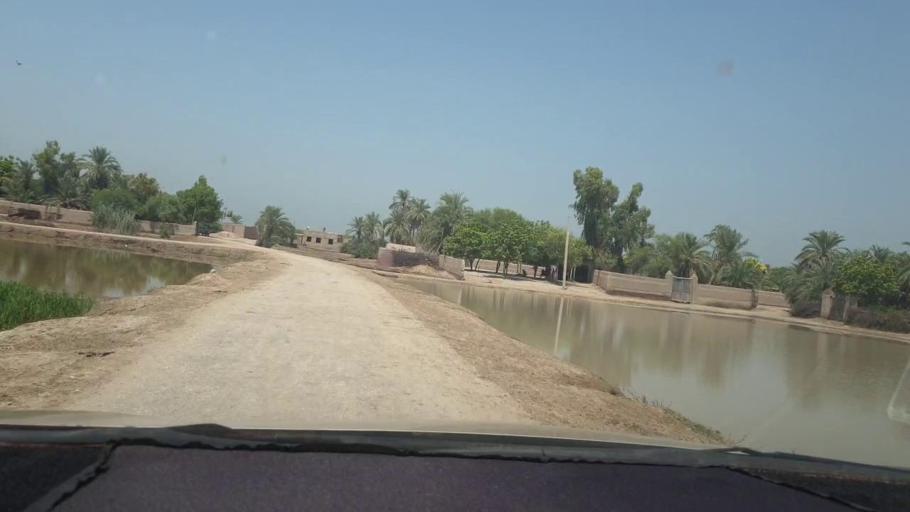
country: PK
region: Sindh
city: Kambar
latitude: 27.6241
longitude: 68.0522
